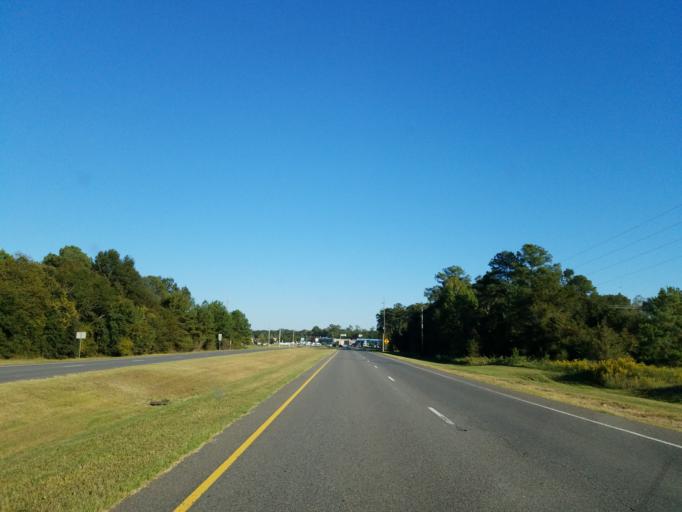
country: US
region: Georgia
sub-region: Lee County
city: Leesburg
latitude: 31.7214
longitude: -84.1763
